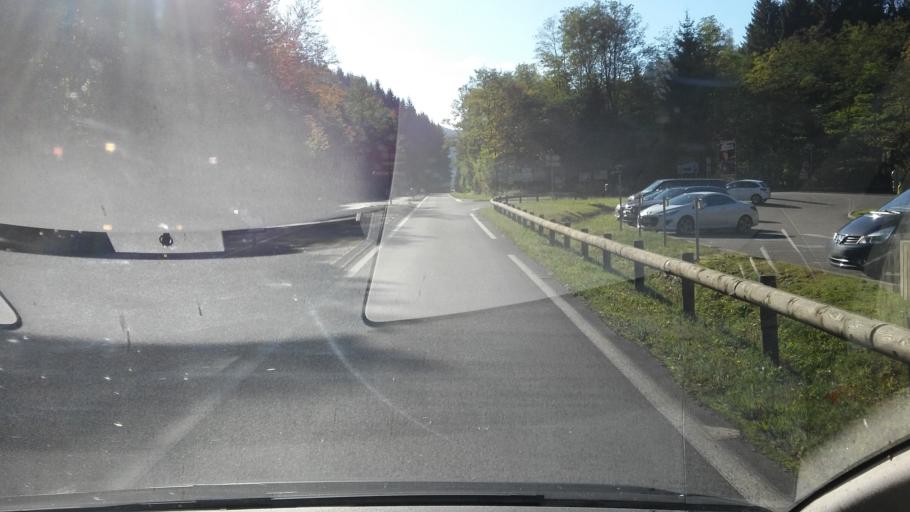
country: FR
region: Lorraine
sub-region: Departement de la Moselle
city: Dabo
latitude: 48.7117
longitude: 7.2174
